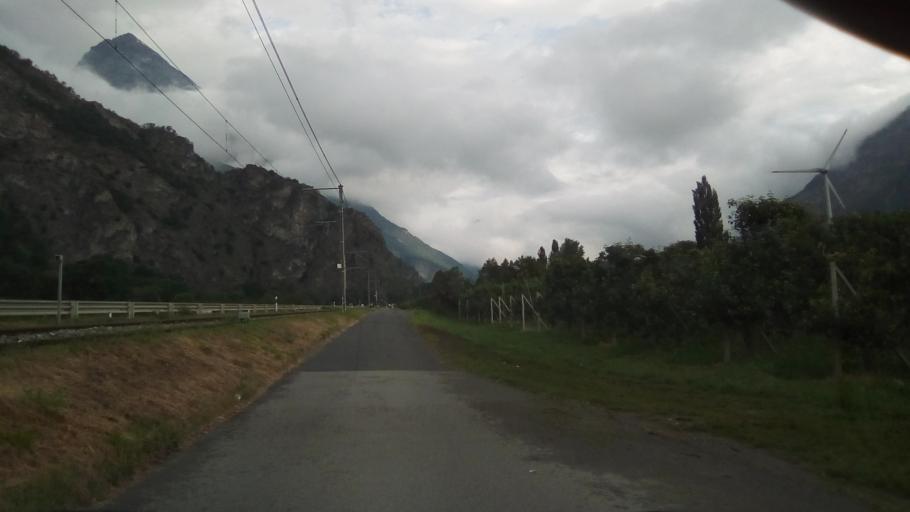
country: CH
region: Valais
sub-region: Saint-Maurice District
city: Vernayaz
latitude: 46.1207
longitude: 7.0523
